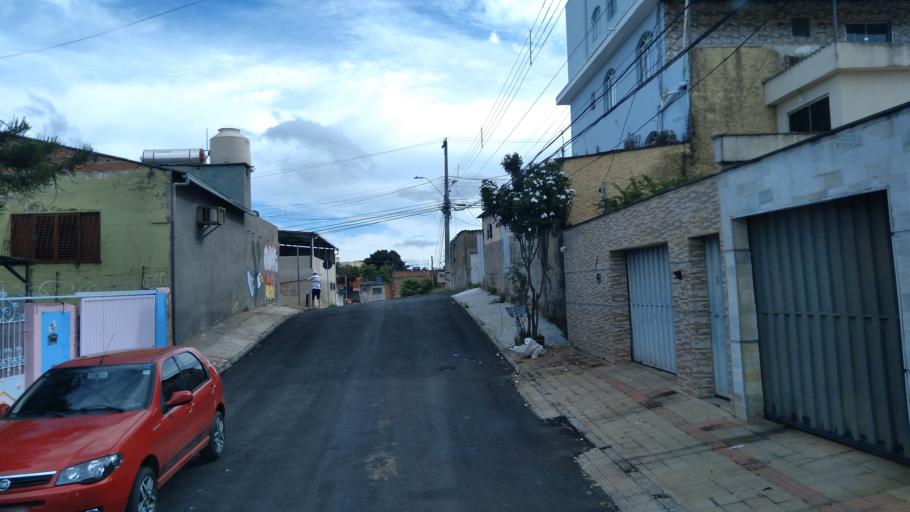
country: BR
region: Minas Gerais
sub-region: Contagem
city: Contagem
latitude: -19.9125
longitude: -43.9982
